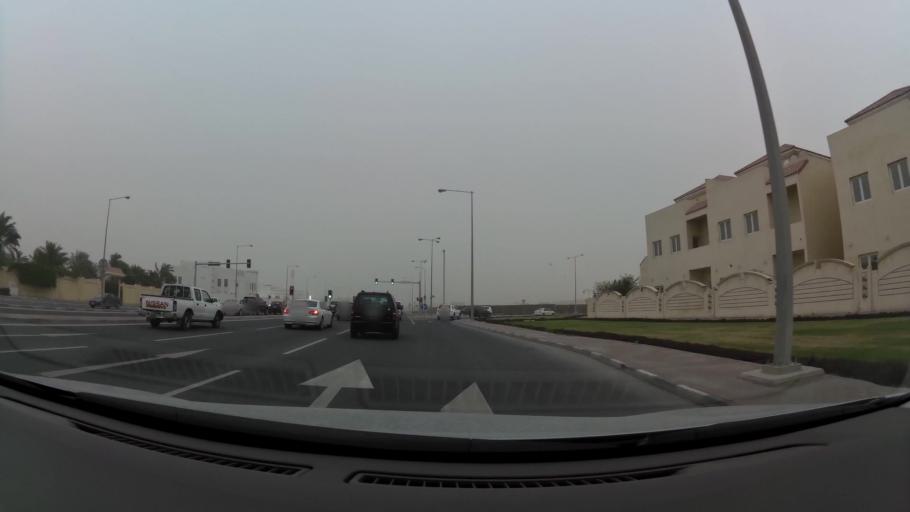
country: QA
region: Baladiyat ad Dawhah
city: Doha
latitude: 25.2459
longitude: 51.4918
